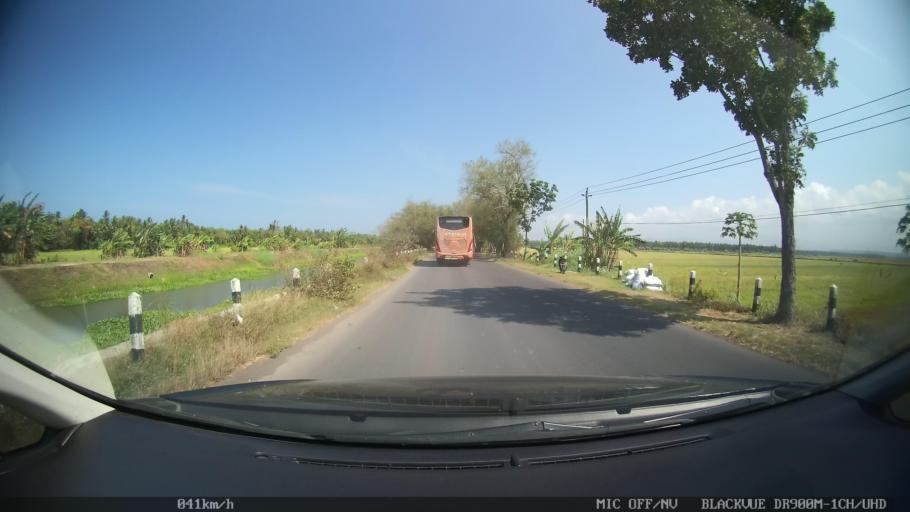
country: ID
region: Daerah Istimewa Yogyakarta
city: Srandakan
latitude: -7.9473
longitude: 110.1789
